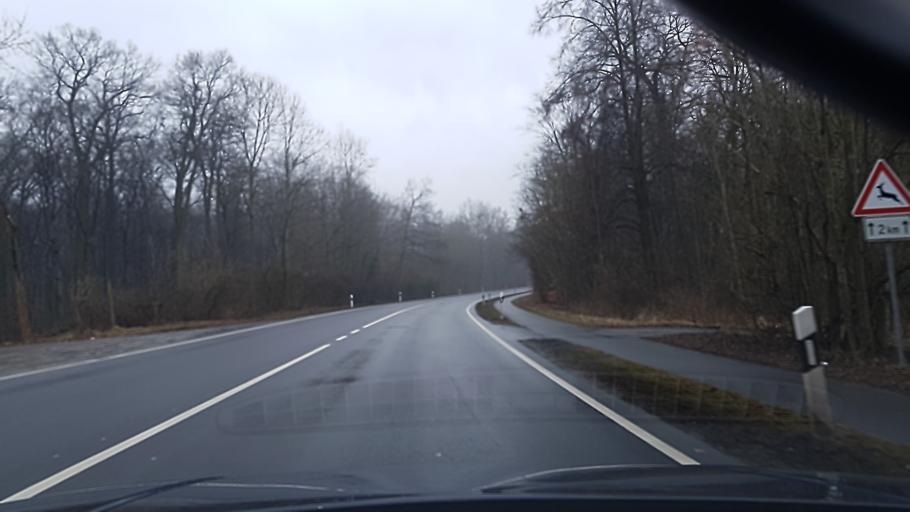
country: DE
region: Lower Saxony
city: Leiferde
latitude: 52.1843
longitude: 10.4567
